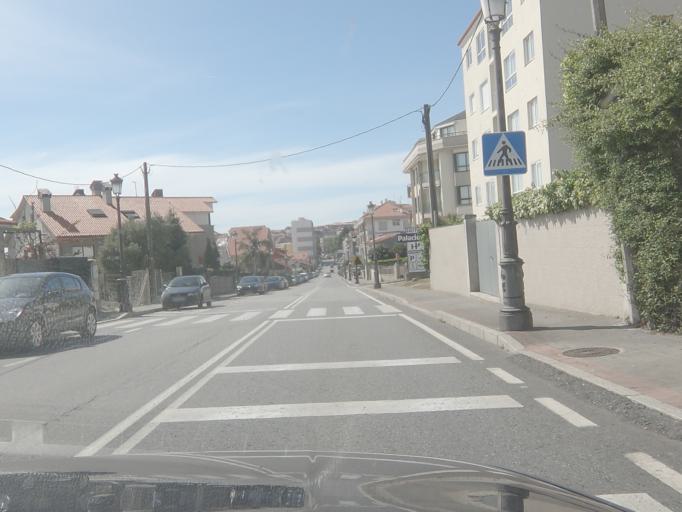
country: ES
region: Galicia
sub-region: Provincia de Pontevedra
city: Sanxenxo
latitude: 42.3990
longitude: -8.7946
